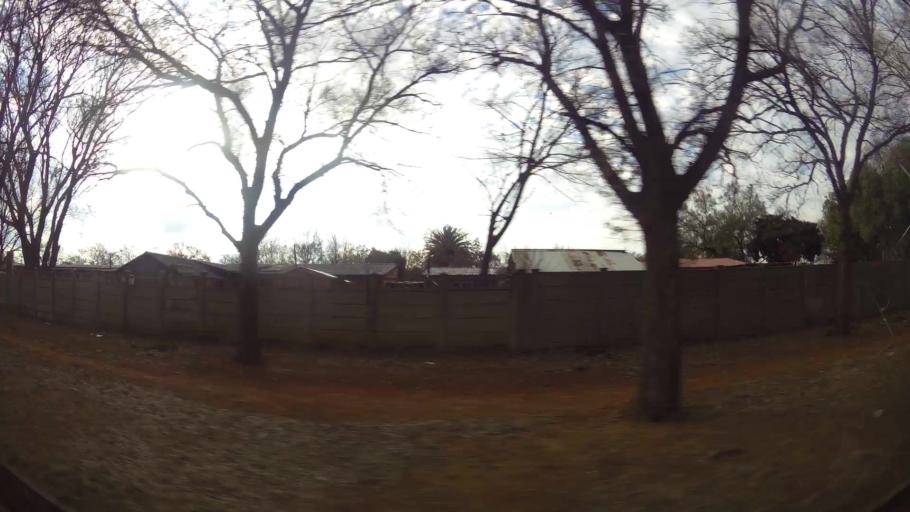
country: ZA
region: Orange Free State
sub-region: Fezile Dabi District Municipality
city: Sasolburg
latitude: -26.8182
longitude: 27.8150
